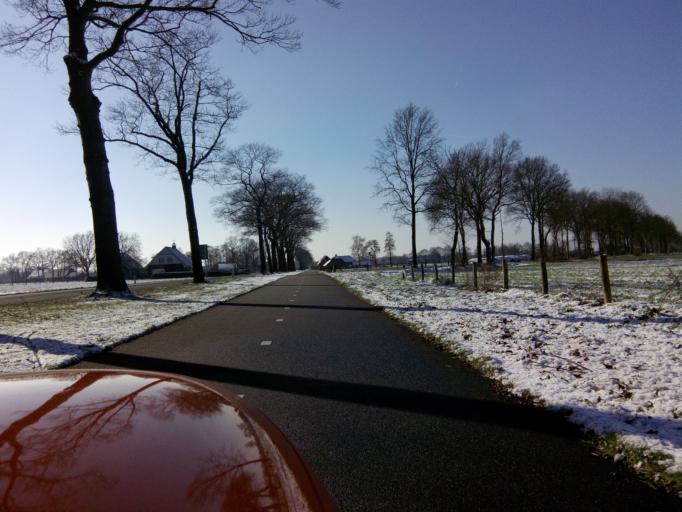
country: NL
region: Gelderland
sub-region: Gemeente Barneveld
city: Stroe
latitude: 52.1745
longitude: 5.6919
